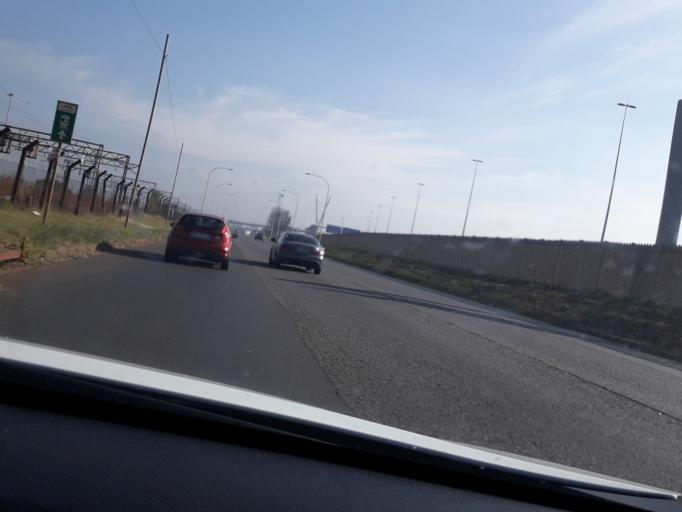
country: ZA
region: Gauteng
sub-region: City of Johannesburg Metropolitan Municipality
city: Modderfontein
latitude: -26.1409
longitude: 28.2202
